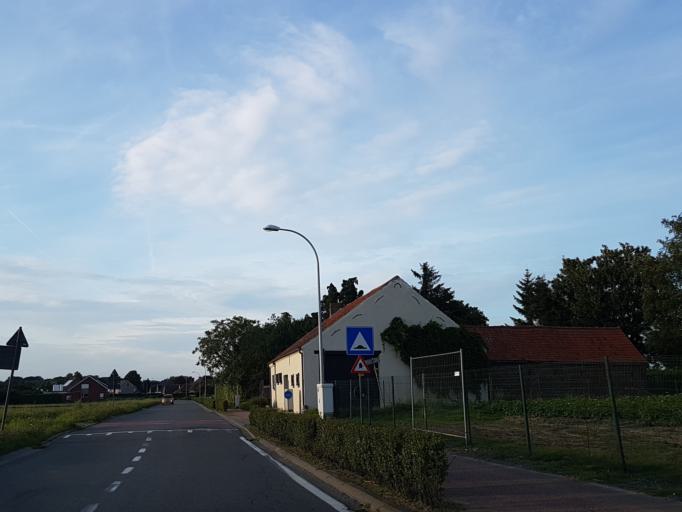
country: BE
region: Flanders
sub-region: Provincie Vlaams-Brabant
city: Londerzeel
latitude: 50.9959
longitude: 4.2840
